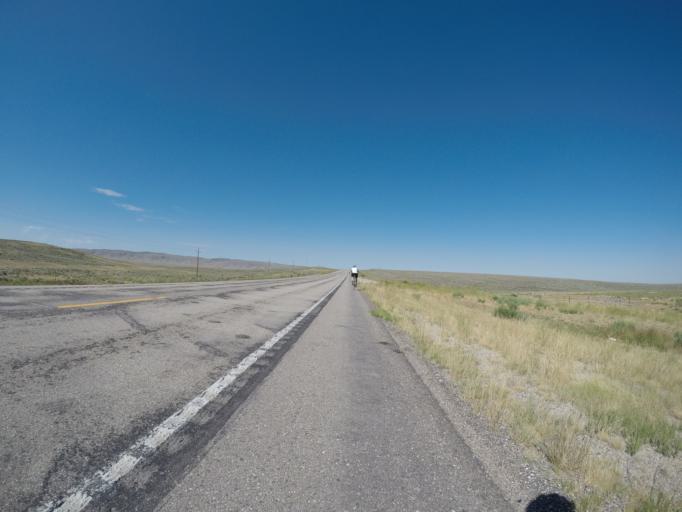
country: US
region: Wyoming
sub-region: Carbon County
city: Saratoga
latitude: 41.8199
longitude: -106.6571
